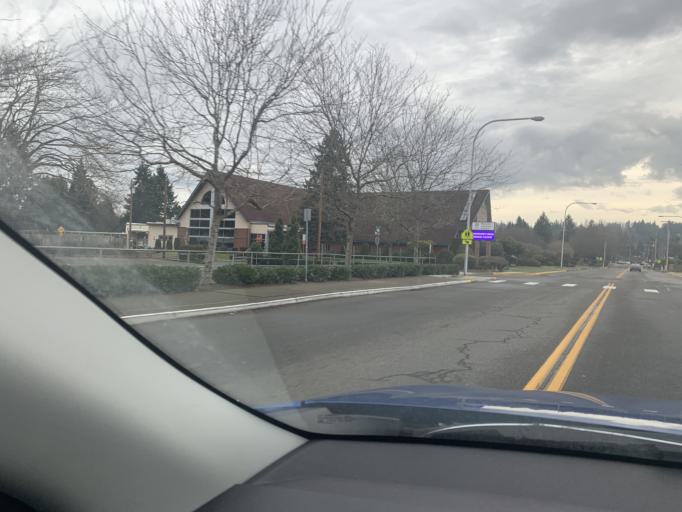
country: US
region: Washington
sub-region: King County
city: Auburn
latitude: 47.3110
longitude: -122.2201
